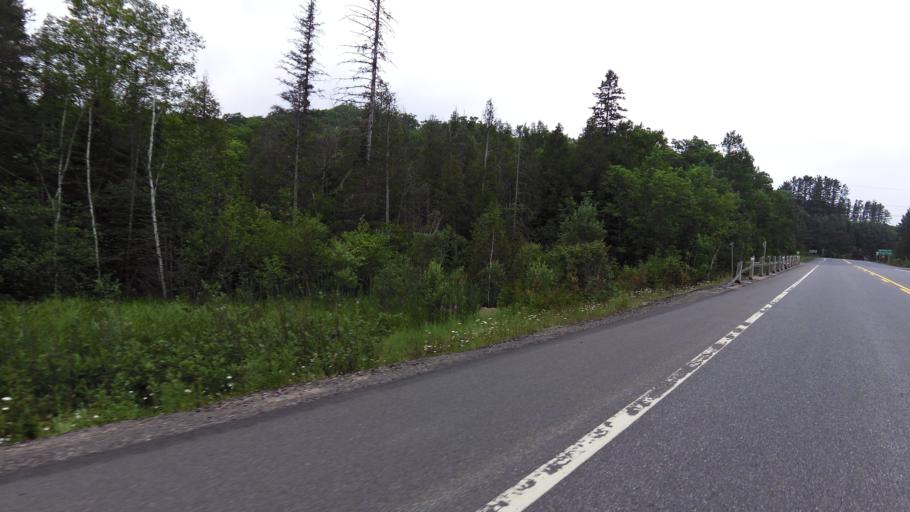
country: CA
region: Ontario
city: Huntsville
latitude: 45.3755
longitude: -78.9273
